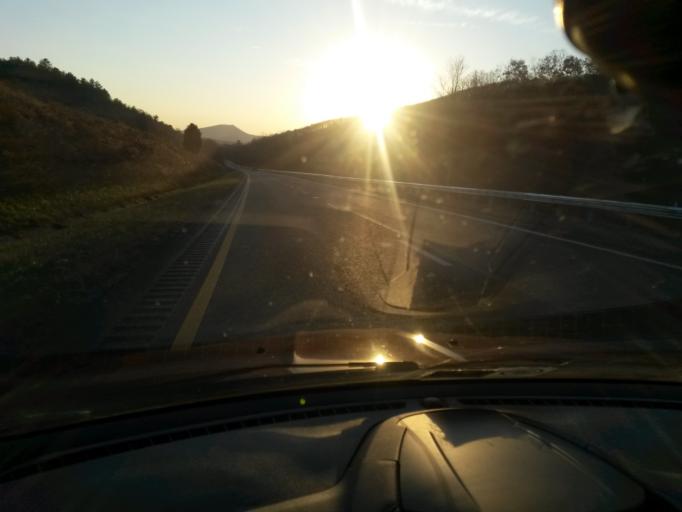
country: US
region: Virginia
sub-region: Alleghany County
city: Clifton Forge
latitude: 37.8345
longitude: -79.6502
